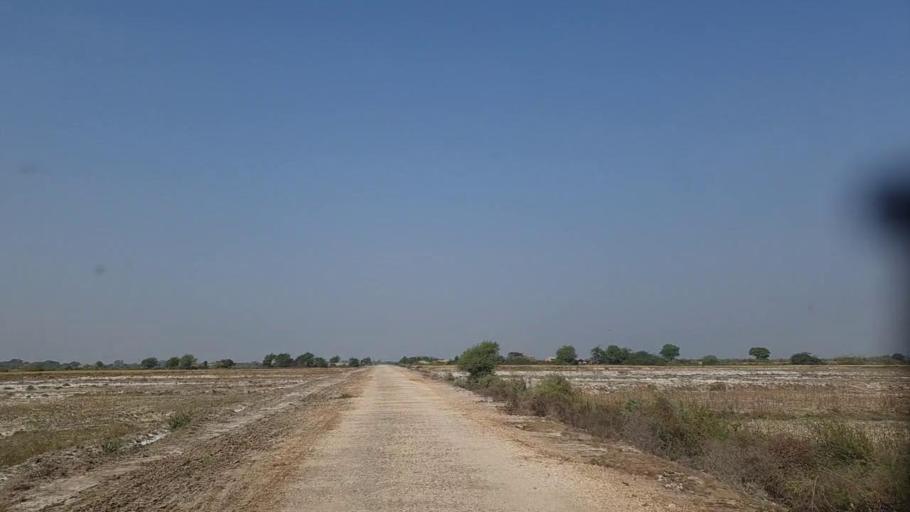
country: PK
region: Sindh
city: Mirpur Batoro
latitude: 24.5837
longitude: 68.1368
